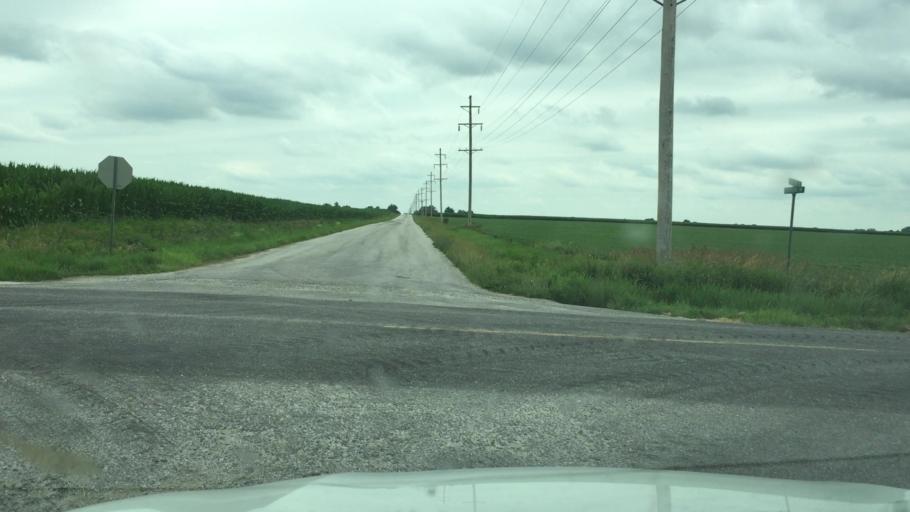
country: US
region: Illinois
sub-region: Hancock County
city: Carthage
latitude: 40.3418
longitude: -91.0823
